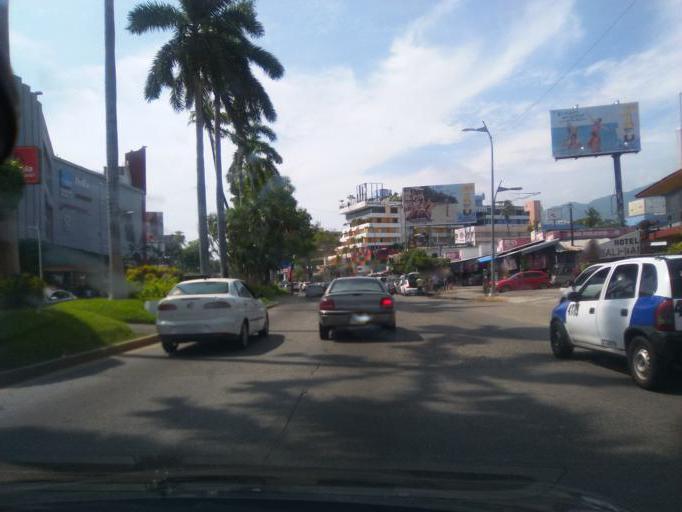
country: MX
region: Guerrero
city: Acapulco de Juarez
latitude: 16.8614
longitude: -99.8761
